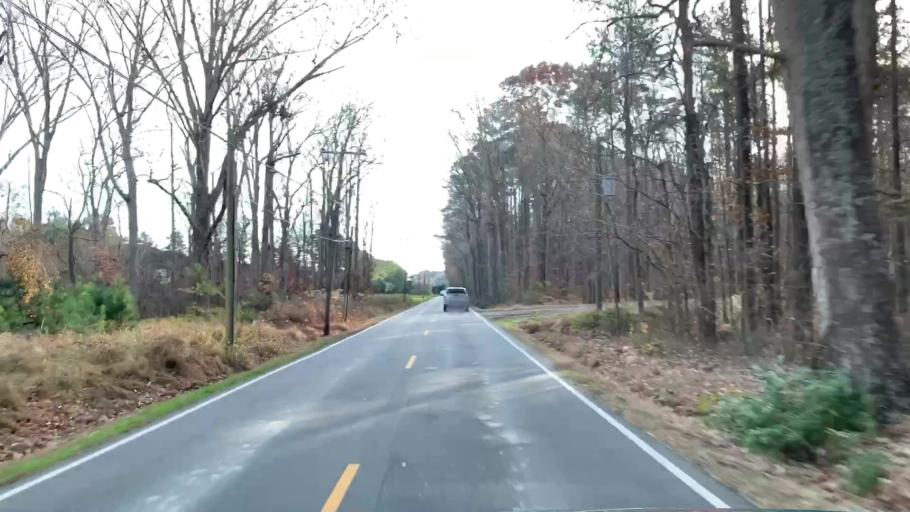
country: US
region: Virginia
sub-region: City of Virginia Beach
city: Virginia Beach
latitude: 36.7256
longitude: -76.0732
